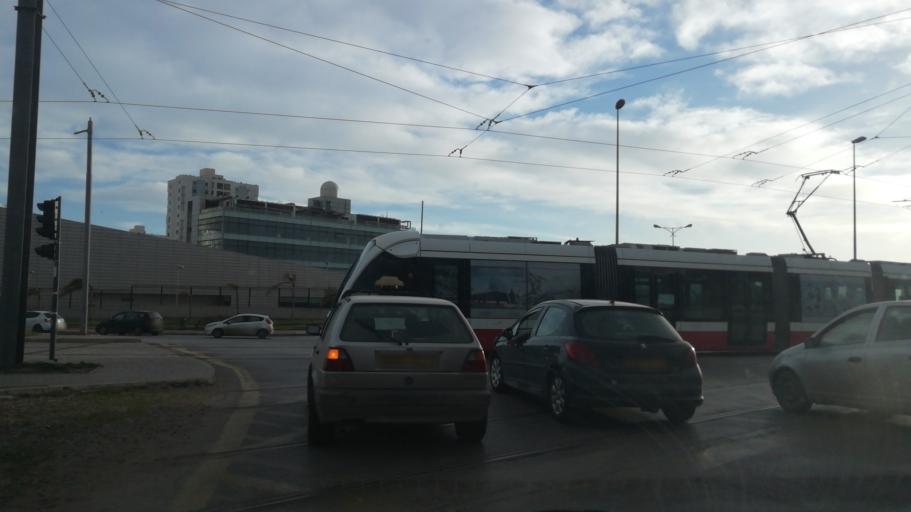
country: DZ
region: Oran
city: Bir el Djir
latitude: 35.7066
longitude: -0.5725
